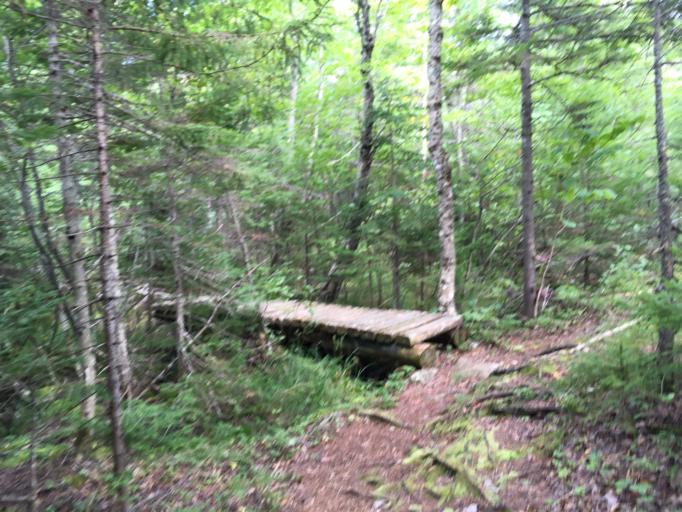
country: US
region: Maine
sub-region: Penobscot County
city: Millinocket
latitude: 45.9207
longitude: -68.8571
